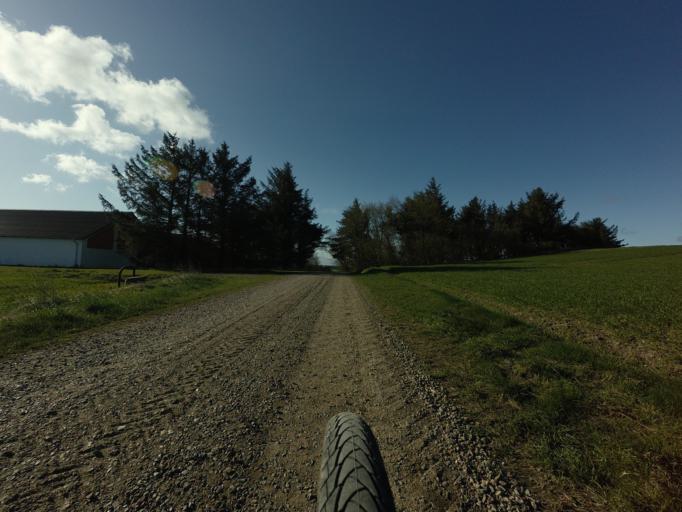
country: DK
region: North Denmark
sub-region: Hjorring Kommune
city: Vra
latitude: 57.3646
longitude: 9.8167
